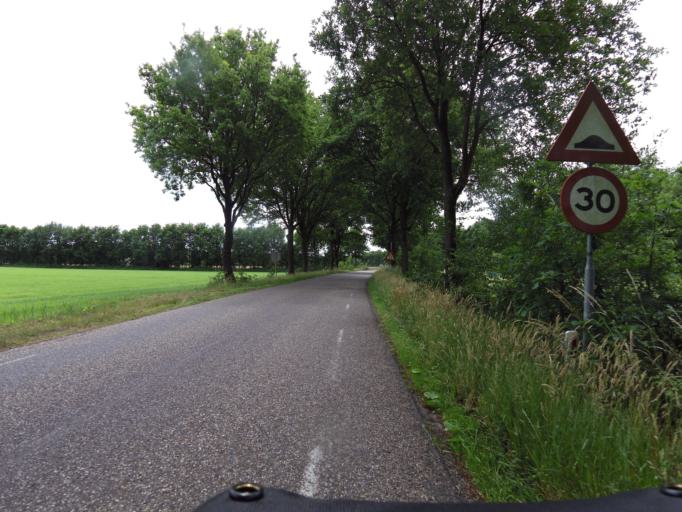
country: NL
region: North Brabant
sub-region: Gemeente Bladel en Netersel
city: Bladel
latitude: 51.4202
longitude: 5.2189
